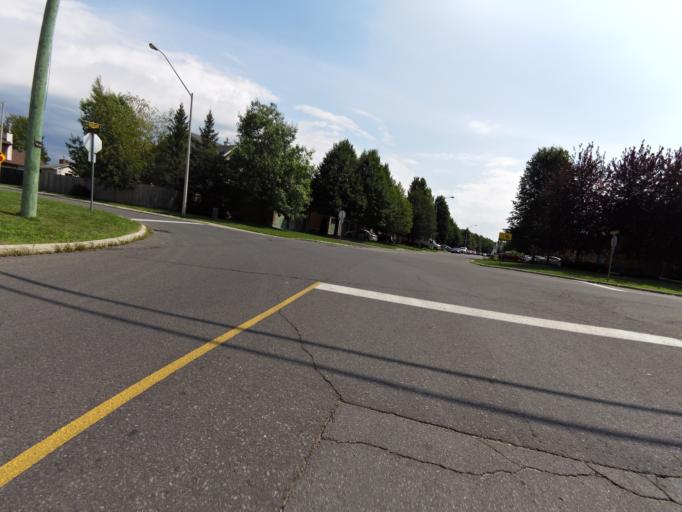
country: CA
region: Quebec
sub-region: Outaouais
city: Gatineau
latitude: 45.4733
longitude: -75.5153
